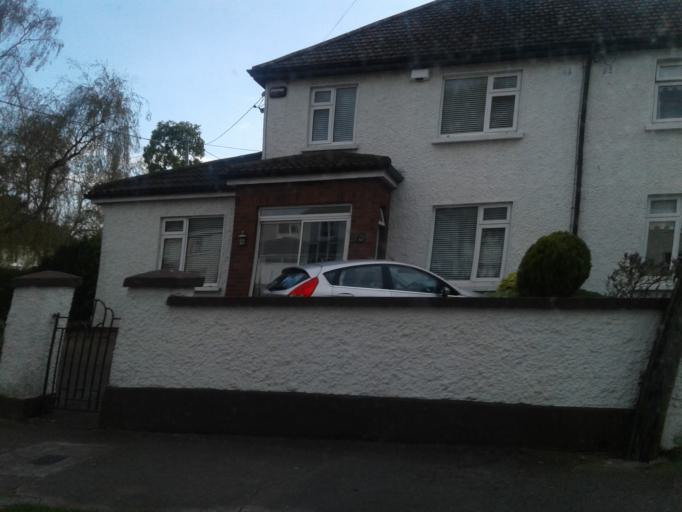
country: IE
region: Leinster
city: Beaumont
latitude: 53.3848
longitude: -6.2329
